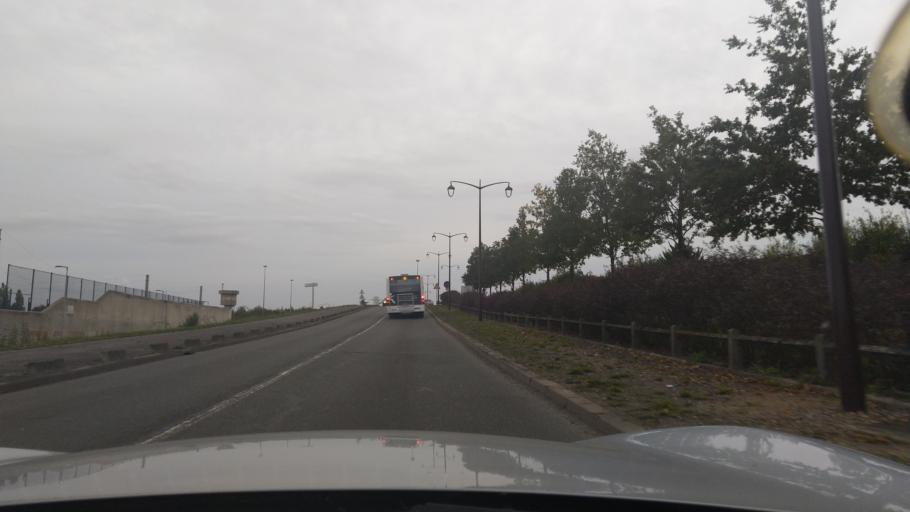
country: FR
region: Ile-de-France
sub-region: Departement de Seine-Saint-Denis
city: Villepinte
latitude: 48.9670
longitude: 2.5519
